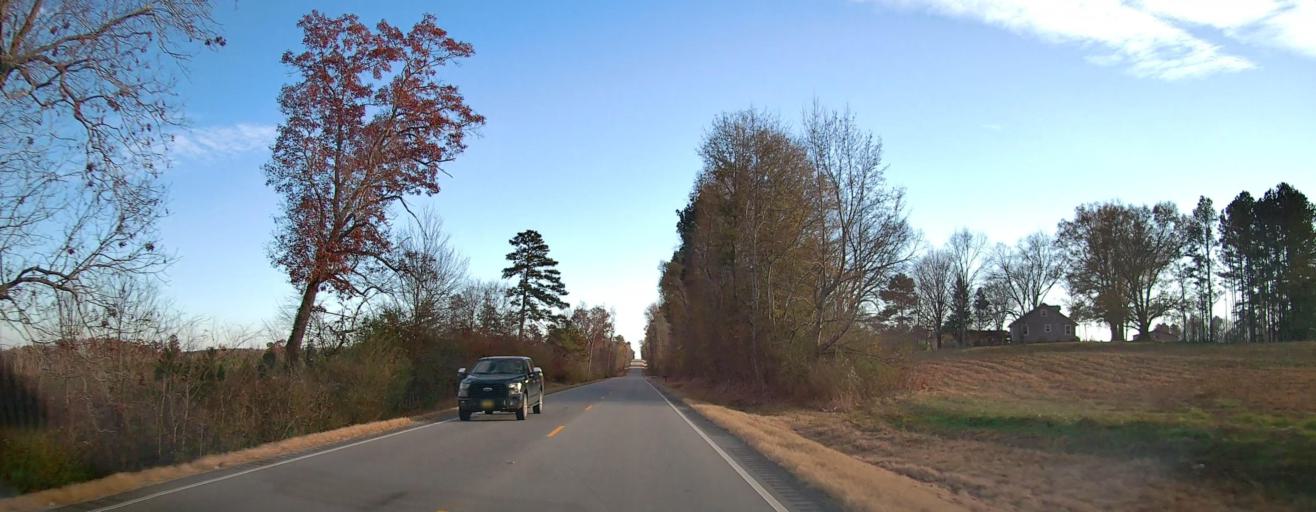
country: US
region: Alabama
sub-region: Marshall County
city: Arab
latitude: 34.2717
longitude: -86.5791
